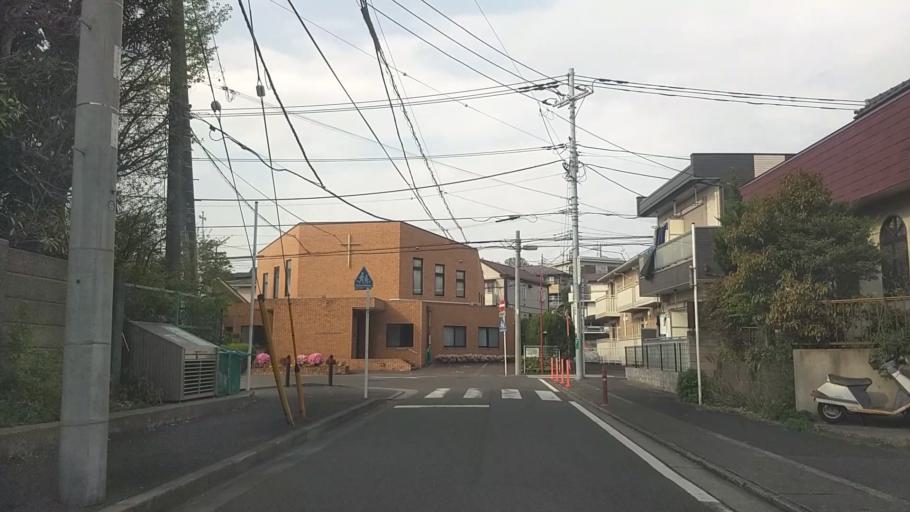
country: JP
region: Kanagawa
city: Kamakura
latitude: 35.3663
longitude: 139.5557
